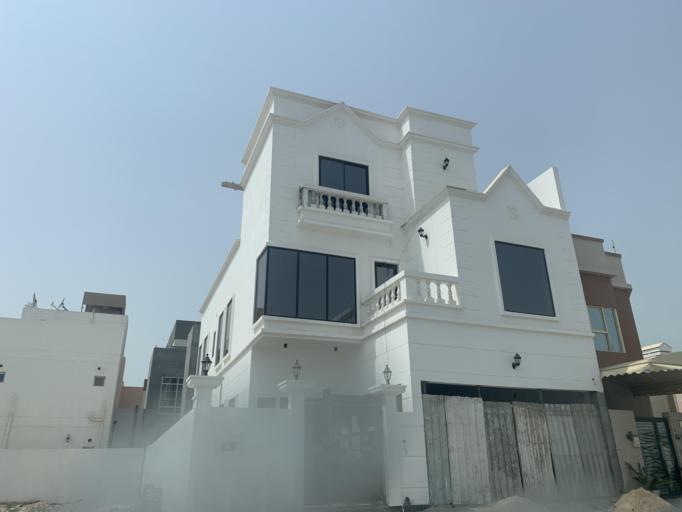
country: BH
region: Manama
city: Jidd Hafs
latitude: 26.2017
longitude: 50.4685
